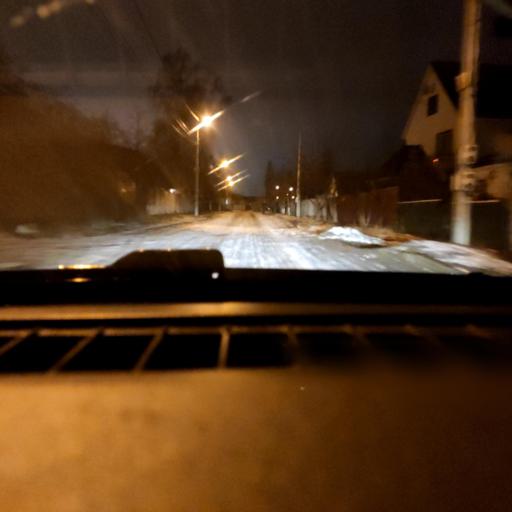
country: RU
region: Voronezj
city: Podgornoye
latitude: 51.7326
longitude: 39.1541
